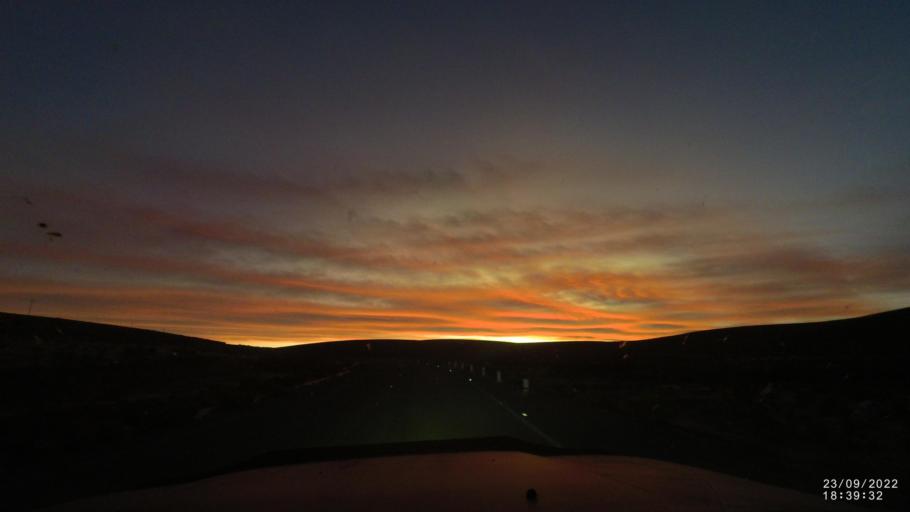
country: BO
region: Oruro
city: Challapata
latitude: -19.4196
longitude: -67.3304
